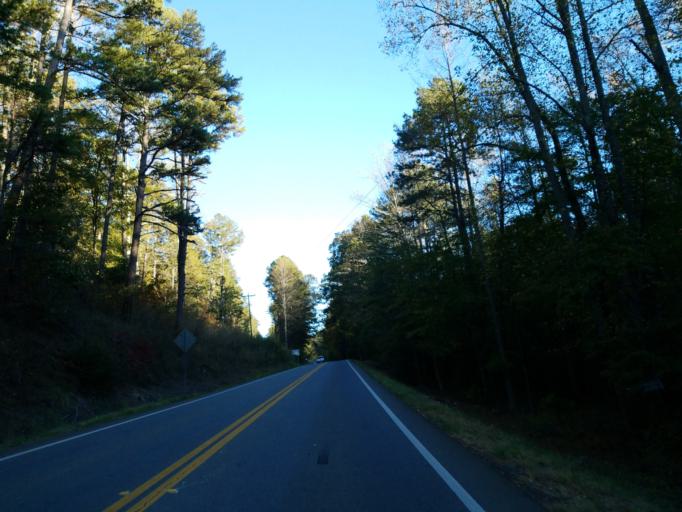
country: US
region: Georgia
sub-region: Dawson County
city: Dawsonville
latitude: 34.4249
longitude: -84.2092
